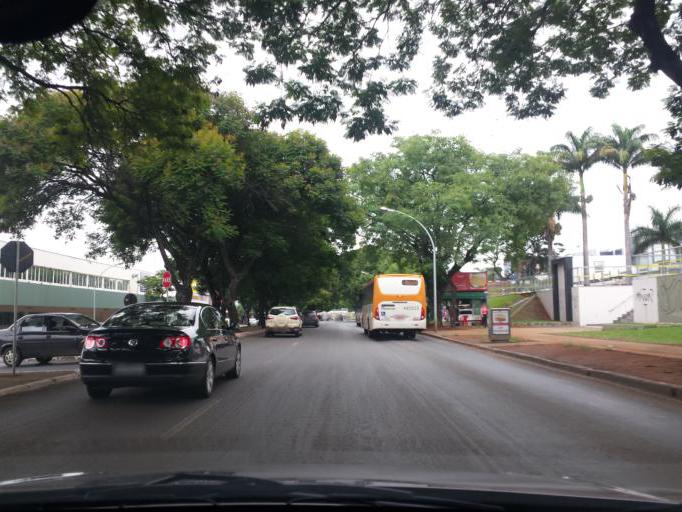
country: BR
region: Federal District
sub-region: Brasilia
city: Brasilia
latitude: -15.8275
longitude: -47.9273
